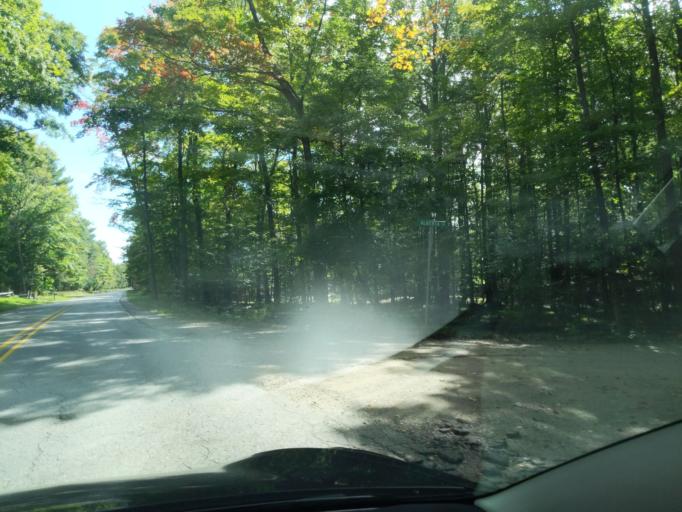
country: US
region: Michigan
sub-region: Antrim County
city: Bellaire
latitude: 45.0716
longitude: -85.3185
